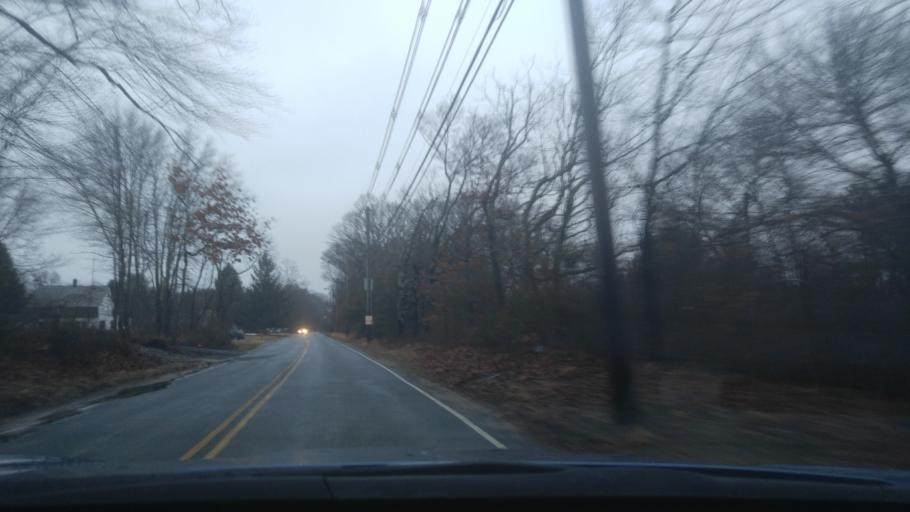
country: US
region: Rhode Island
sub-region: Washington County
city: North Kingstown
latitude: 41.6035
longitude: -71.4802
